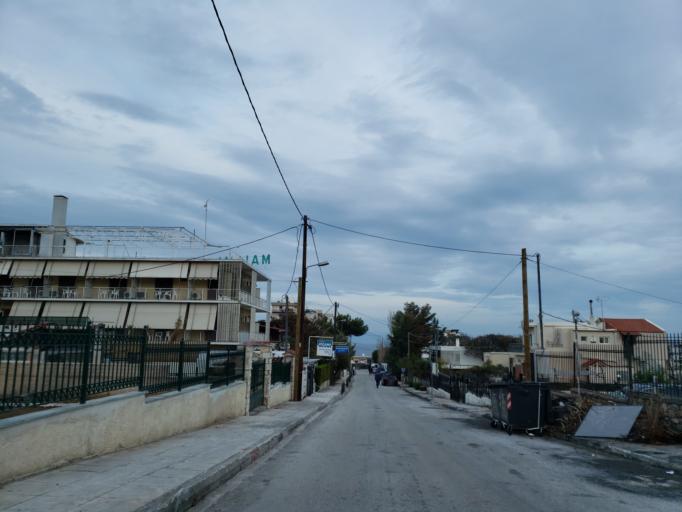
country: GR
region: Attica
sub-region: Nomarchia Anatolikis Attikis
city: Neos Voutzas
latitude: 38.0462
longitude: 23.9960
